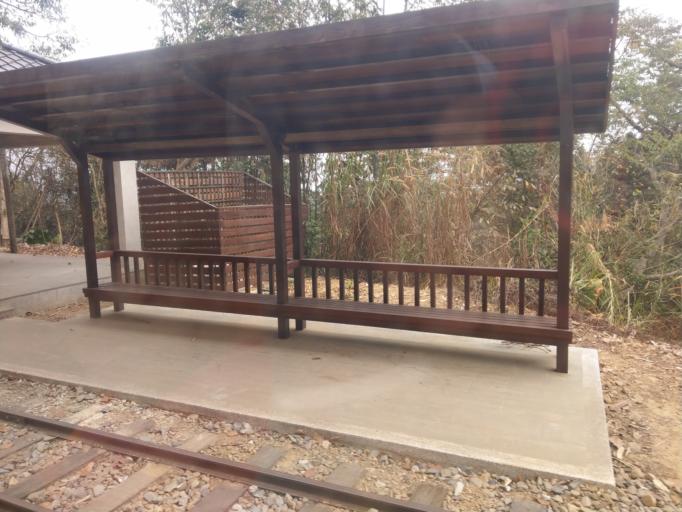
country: TW
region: Taiwan
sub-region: Chiayi
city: Jiayi Shi
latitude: 23.5422
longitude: 120.6201
